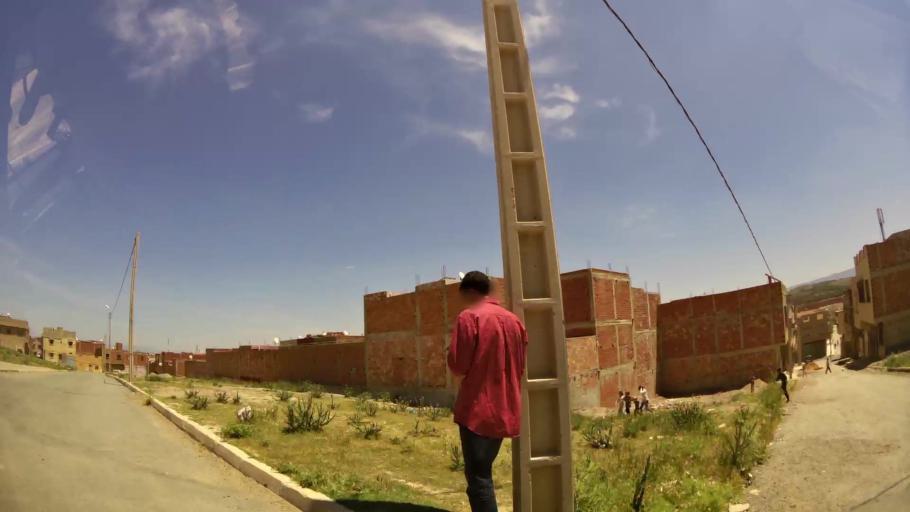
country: MA
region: Oriental
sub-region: Oujda-Angad
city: Oujda
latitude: 34.6539
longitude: -1.9367
